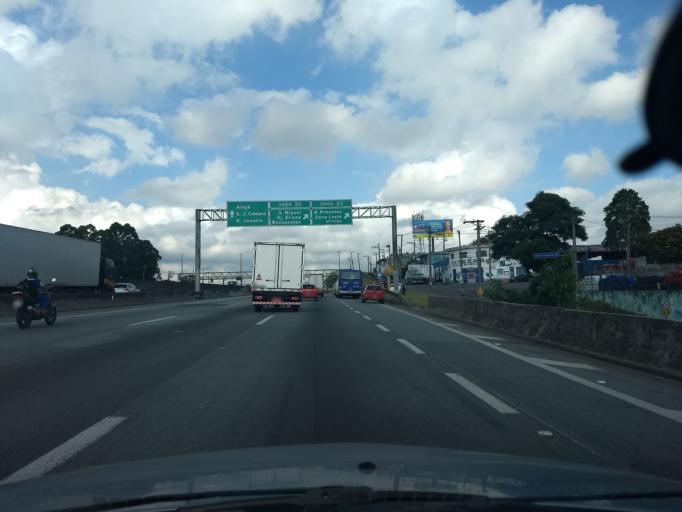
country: BR
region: Sao Paulo
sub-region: Itaquaquecetuba
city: Itaquaquecetuba
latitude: -23.4333
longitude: -46.4215
